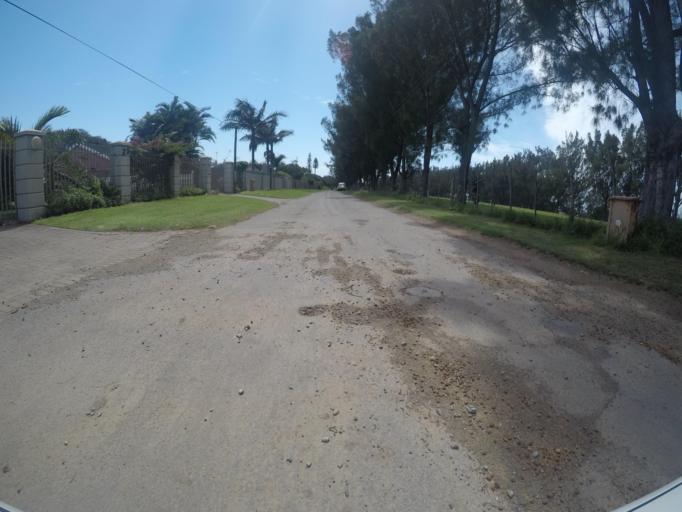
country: ZA
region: Eastern Cape
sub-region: Buffalo City Metropolitan Municipality
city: East London
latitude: -32.9530
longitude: 27.9997
